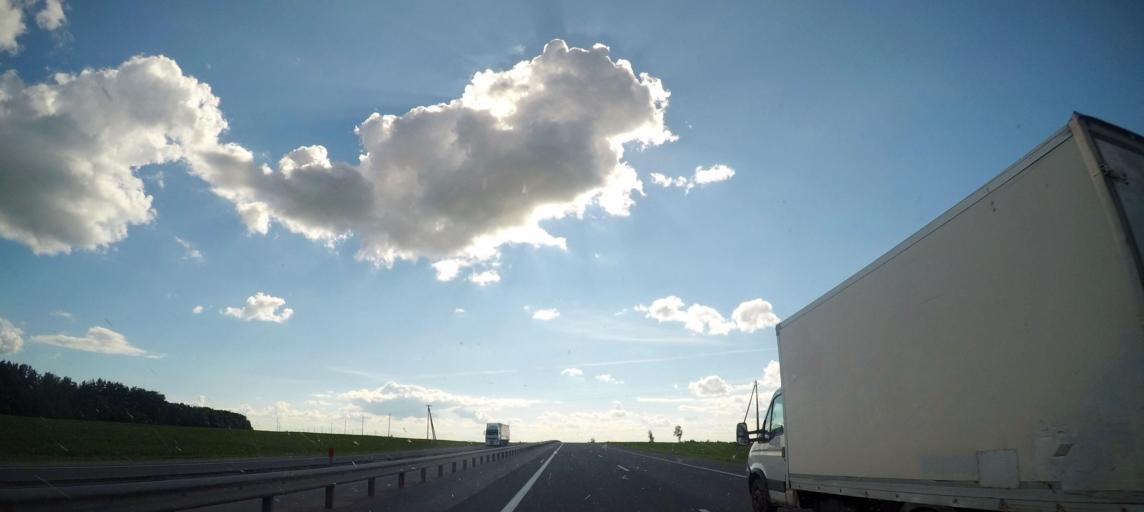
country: BY
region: Grodnenskaya
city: Skidal'
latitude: 53.5760
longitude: 24.3676
